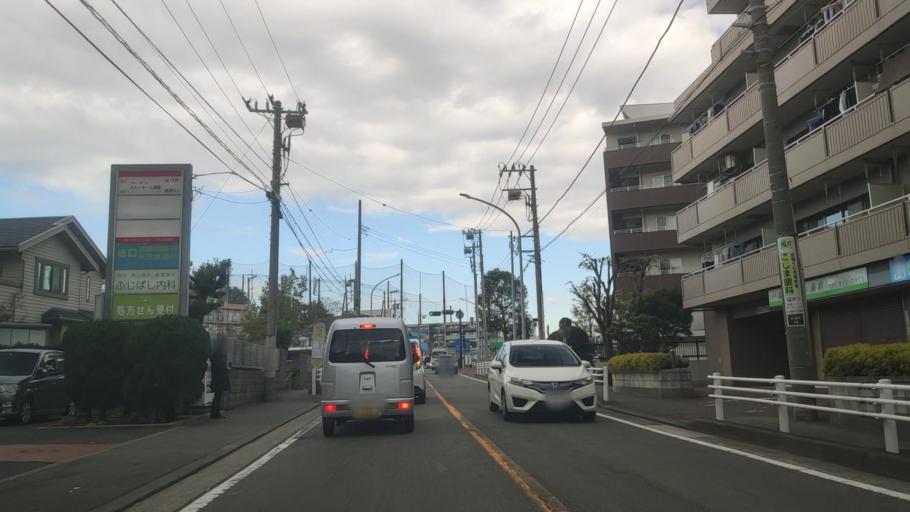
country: JP
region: Kanagawa
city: Fujisawa
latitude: 35.4169
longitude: 139.5393
